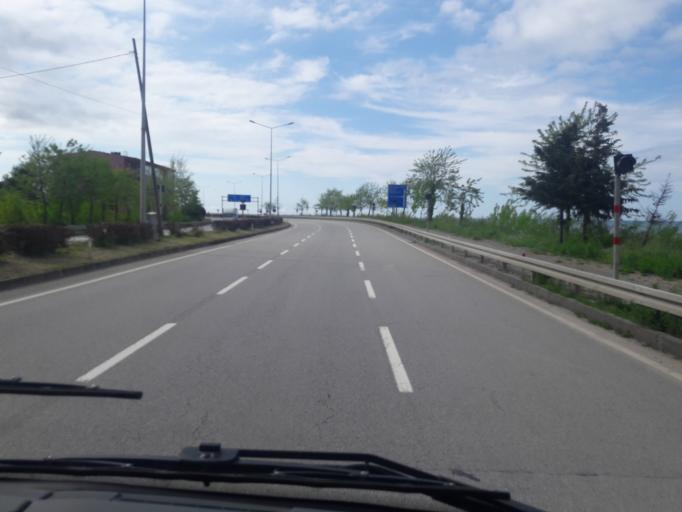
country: TR
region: Giresun
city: Piraziz
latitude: 40.9562
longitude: 38.1192
